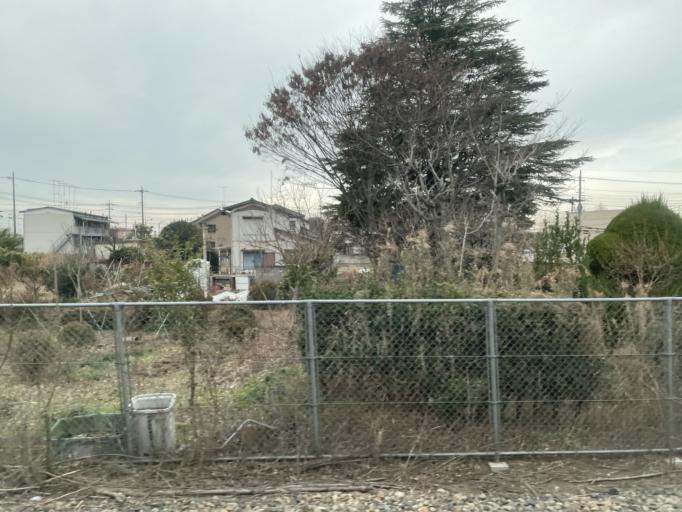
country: JP
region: Ibaraki
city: Koga
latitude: 36.1809
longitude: 139.7135
